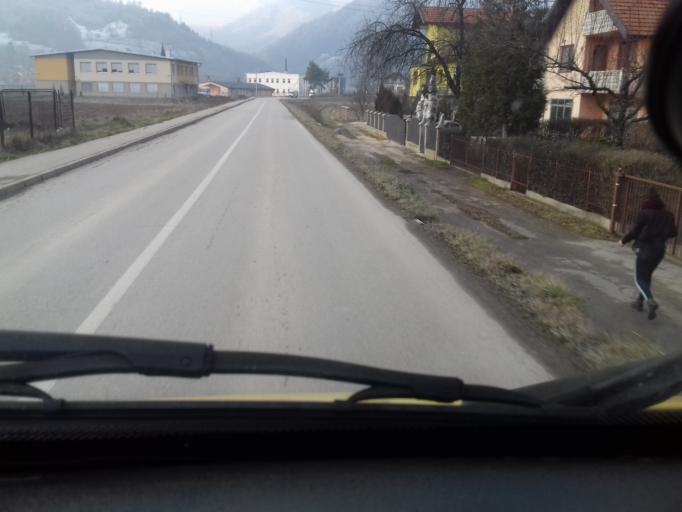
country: BA
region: Federation of Bosnia and Herzegovina
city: Dobrinje
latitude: 44.0501
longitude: 18.1113
